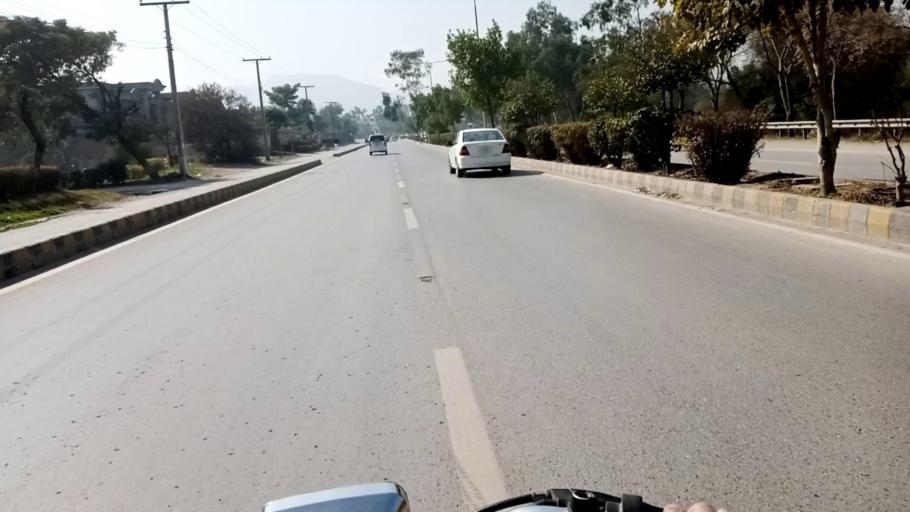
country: PK
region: Khyber Pakhtunkhwa
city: Peshawar
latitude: 33.9658
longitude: 71.4335
